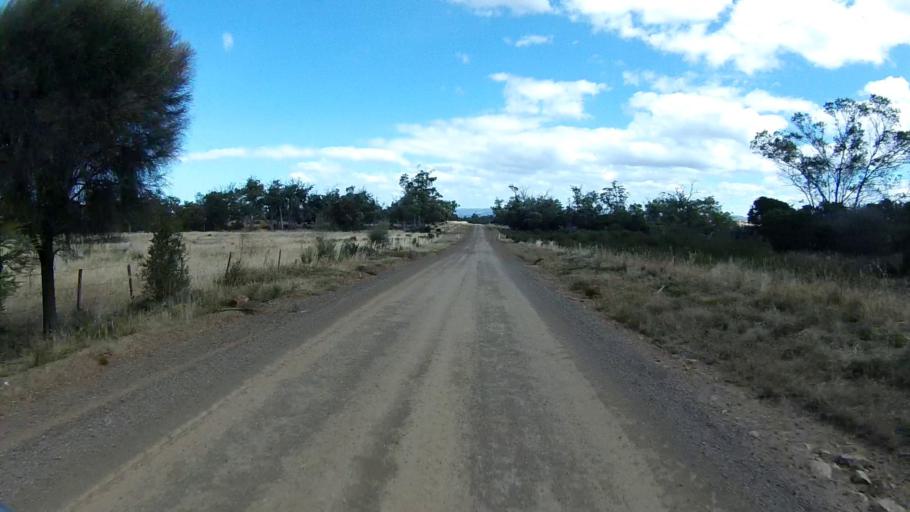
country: AU
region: Tasmania
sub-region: Break O'Day
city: St Helens
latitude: -41.9786
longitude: 148.0686
